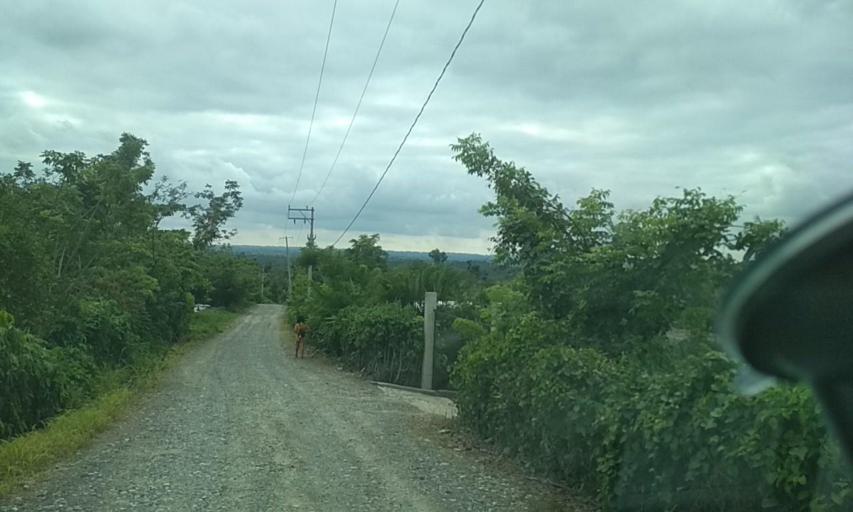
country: MX
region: Veracruz
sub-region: Papantla
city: Polutla
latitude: 20.5861
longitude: -97.2640
